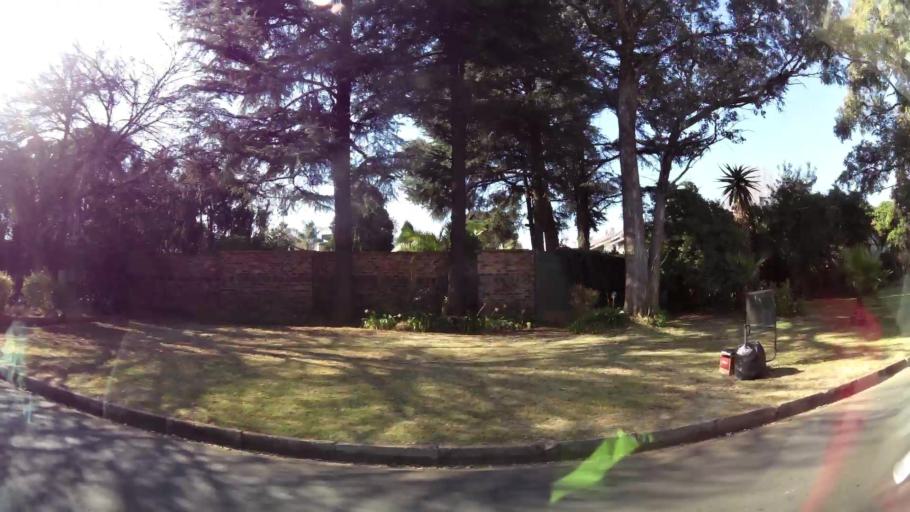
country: ZA
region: Gauteng
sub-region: City of Johannesburg Metropolitan Municipality
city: Modderfontein
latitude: -26.1612
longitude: 28.1351
